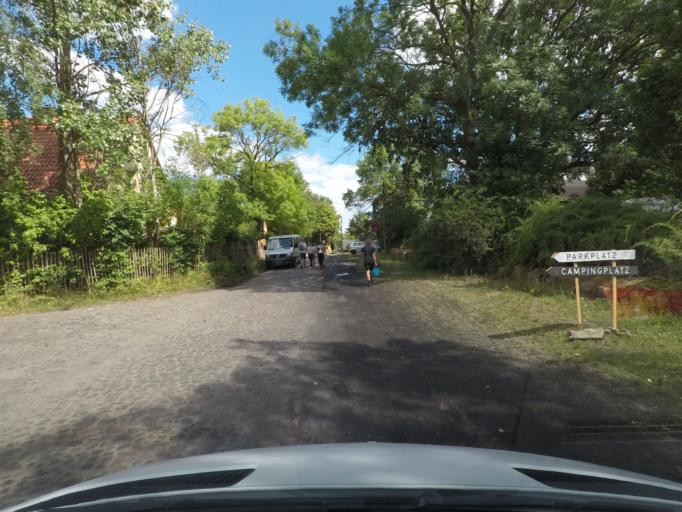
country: DE
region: Brandenburg
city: Brussow
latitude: 53.3654
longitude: 14.1262
